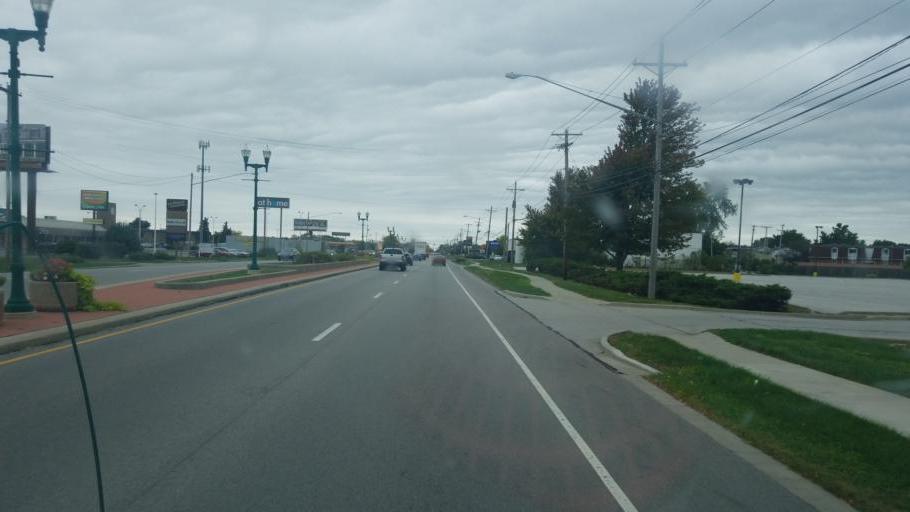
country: US
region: Ohio
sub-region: Lucas County
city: Maumee
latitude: 41.5969
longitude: -83.6645
